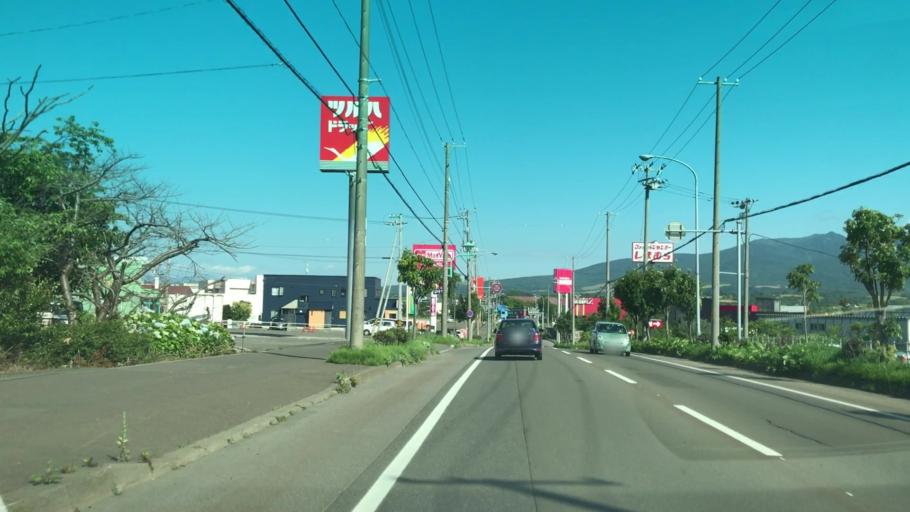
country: JP
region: Hokkaido
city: Iwanai
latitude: 42.9825
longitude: 140.5364
